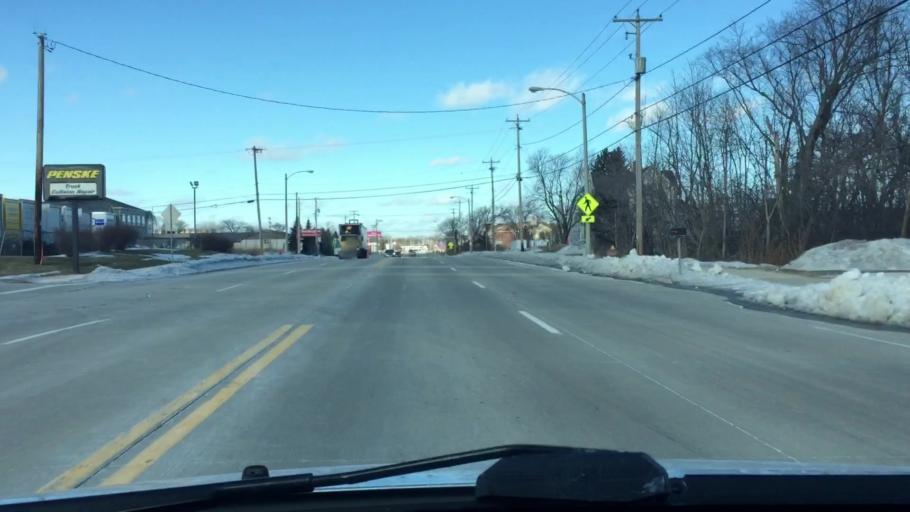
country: US
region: Wisconsin
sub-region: Milwaukee County
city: Greendale
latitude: 42.9237
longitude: -87.9305
